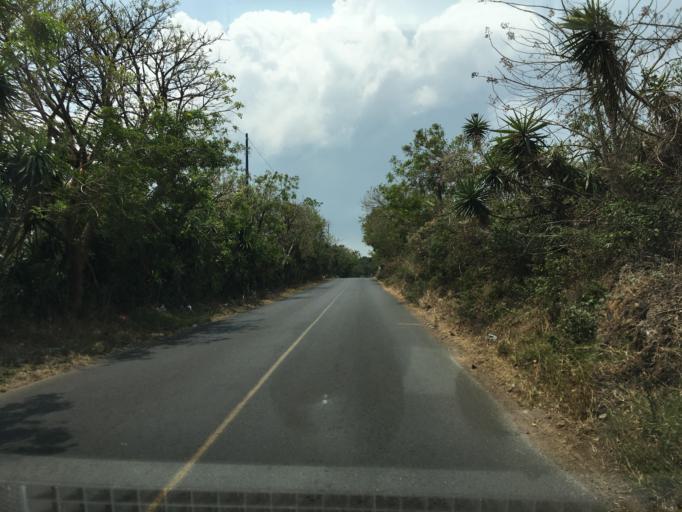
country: GT
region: Escuintla
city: San Vicente Pacaya
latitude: 14.3555
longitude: -90.5722
